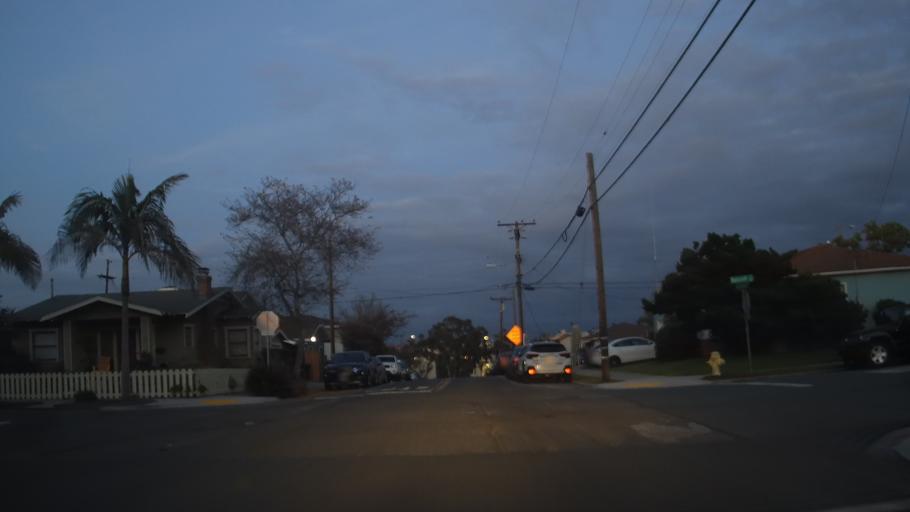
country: US
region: California
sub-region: San Diego County
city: San Diego
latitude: 32.7474
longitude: -117.1240
